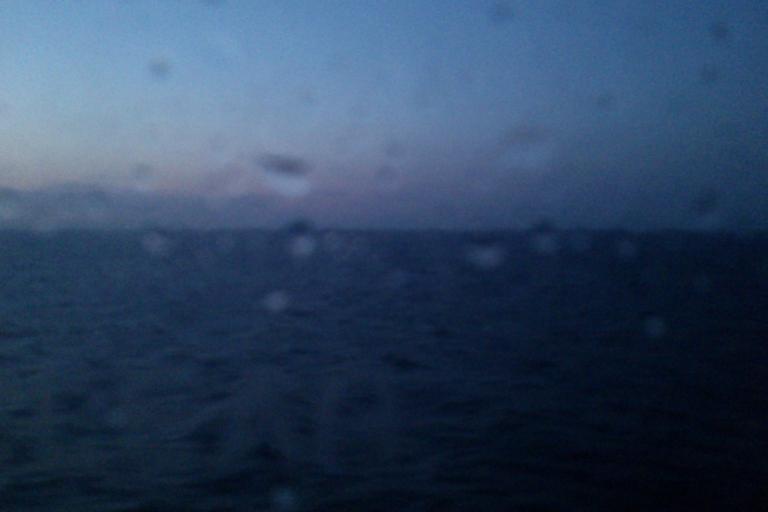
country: JP
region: Ishikawa
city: Kanazawa-shi
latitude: 37.0352
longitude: 135.9930
